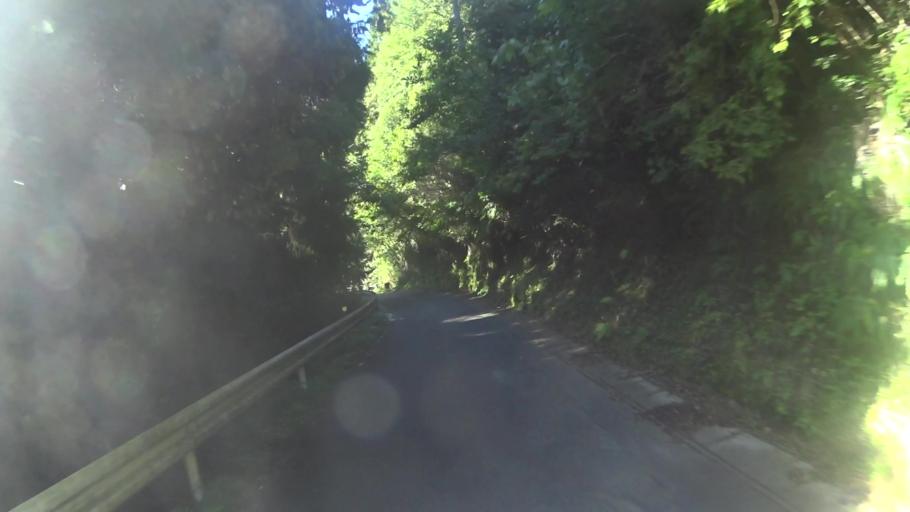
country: JP
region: Kyoto
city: Uji
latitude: 34.8263
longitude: 135.8840
